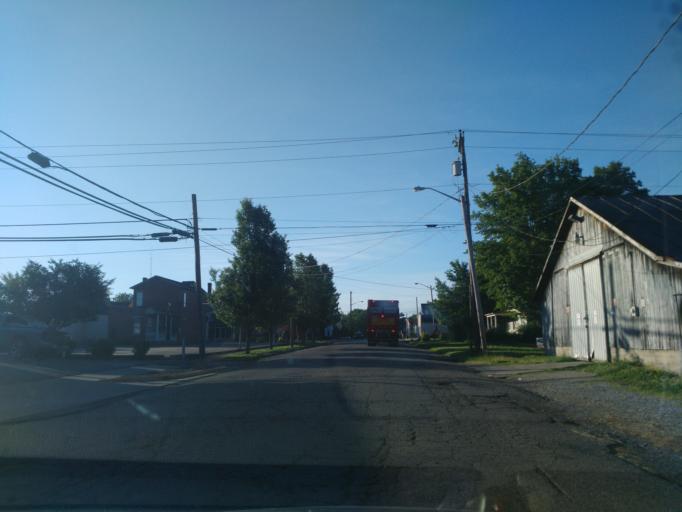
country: US
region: Ohio
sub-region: Pike County
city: Waverly
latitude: 39.1258
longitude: -82.9864
